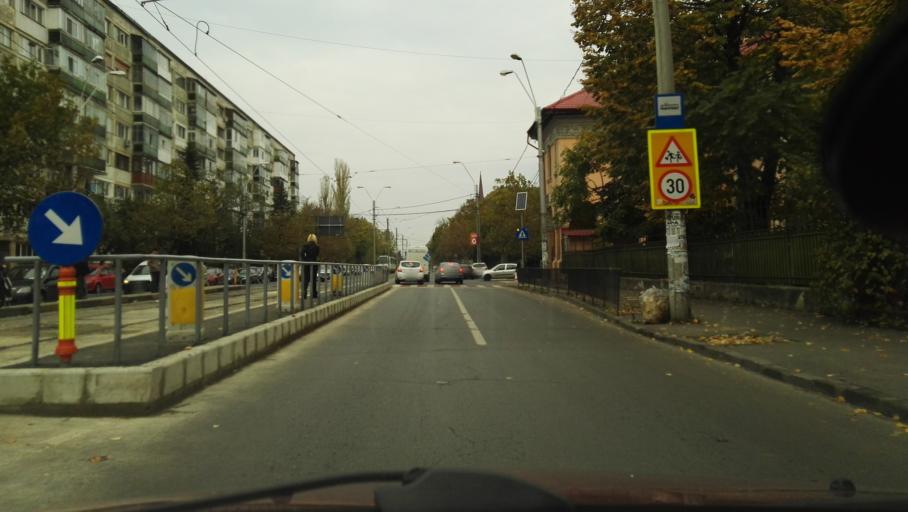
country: RO
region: Bucuresti
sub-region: Municipiul Bucuresti
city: Bucuresti
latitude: 44.4060
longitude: 26.0951
